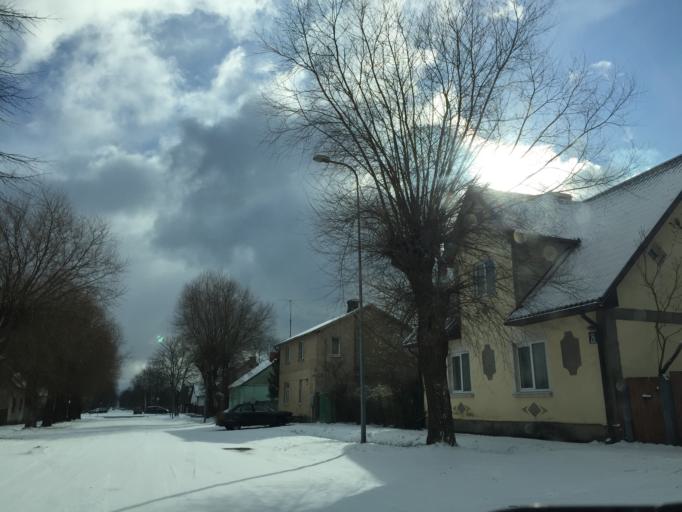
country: LV
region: Ventspils
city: Ventspils
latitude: 57.3832
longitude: 21.5623
